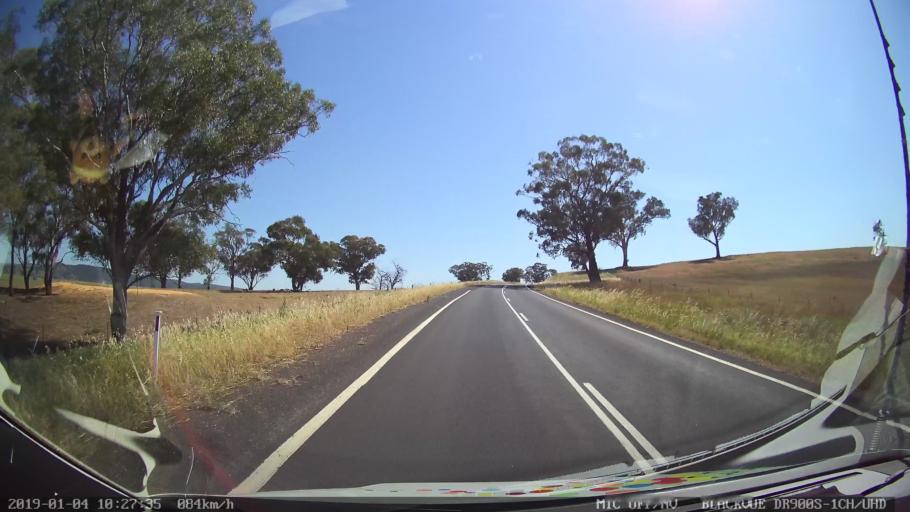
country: AU
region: New South Wales
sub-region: Cabonne
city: Canowindra
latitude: -33.3687
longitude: 148.5997
